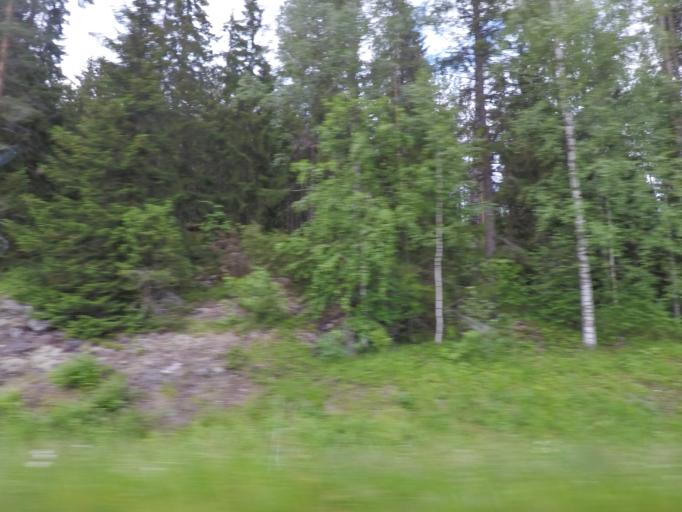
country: FI
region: Paijanne Tavastia
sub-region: Lahti
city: Hollola
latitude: 60.8430
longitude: 25.4945
